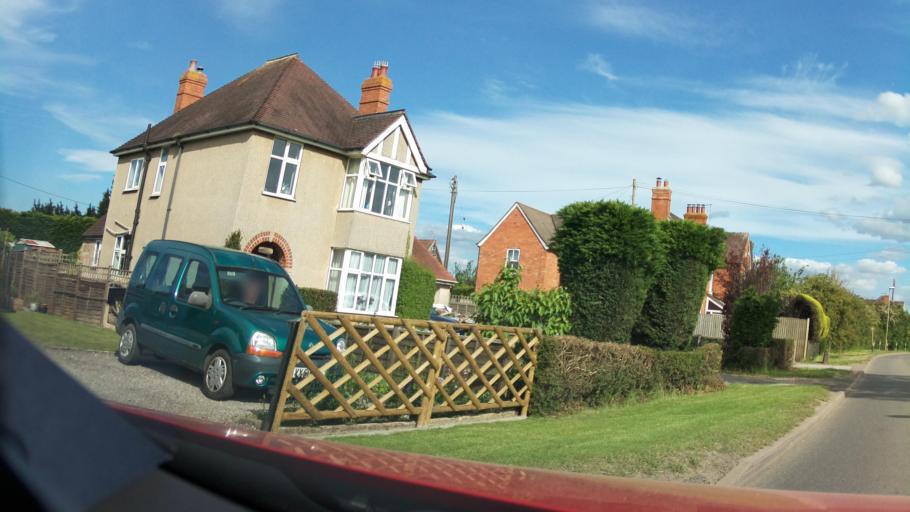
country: GB
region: England
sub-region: Worcestershire
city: Badsey
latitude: 52.0884
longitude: -1.8594
